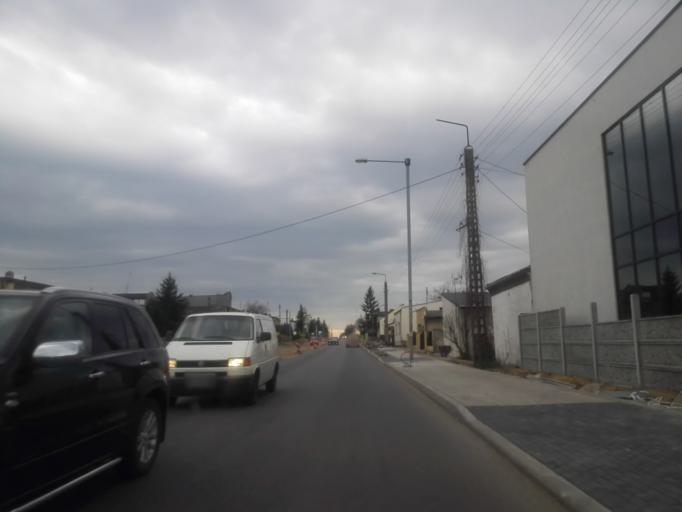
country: PL
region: Silesian Voivodeship
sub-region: Czestochowa
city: Czestochowa
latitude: 50.8396
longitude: 19.1592
